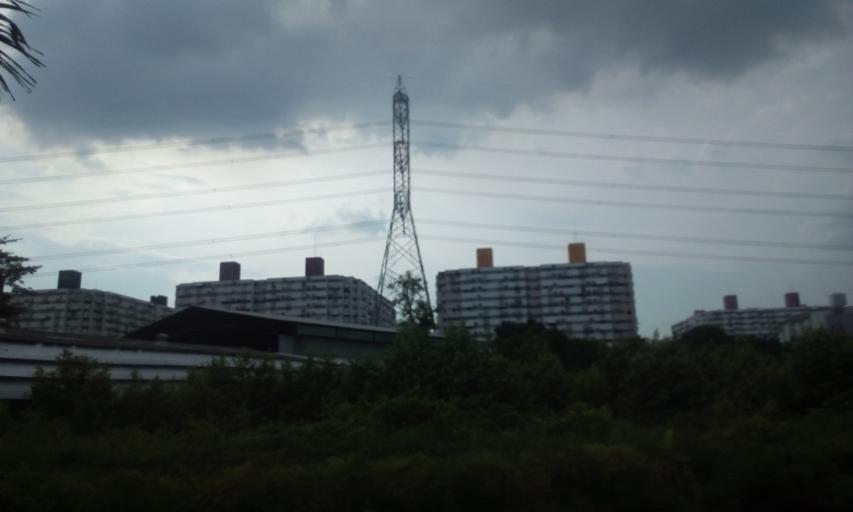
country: TH
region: Bangkok
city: Don Mueang
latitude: 13.9146
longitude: 100.5585
